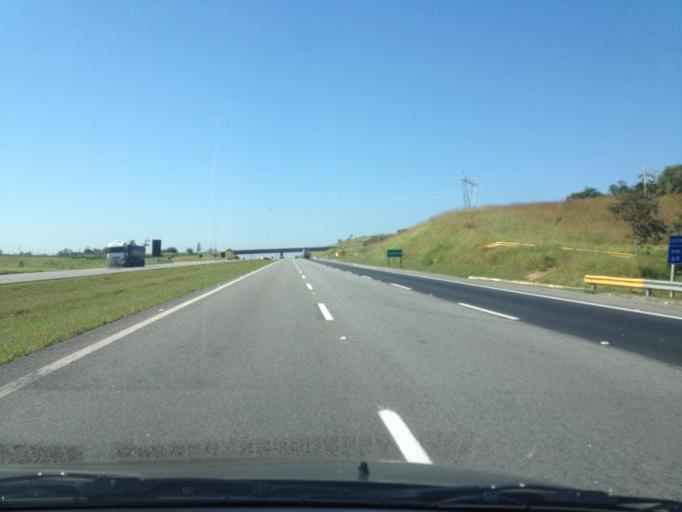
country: BR
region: Sao Paulo
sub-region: Guararema
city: Guararema
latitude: -23.3594
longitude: -46.1047
